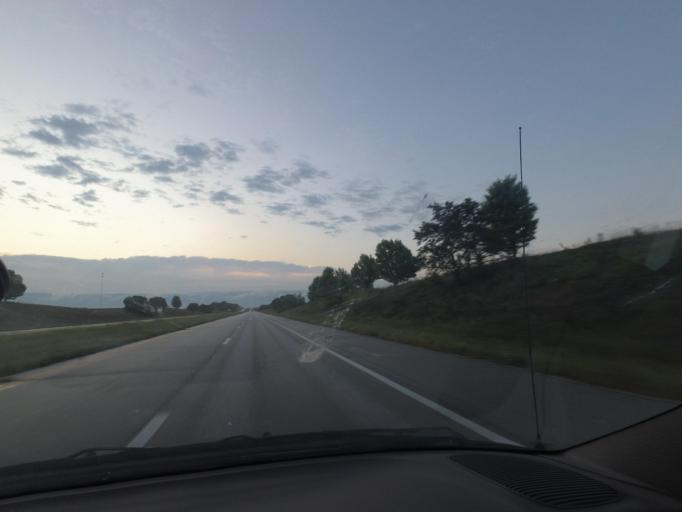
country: US
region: Missouri
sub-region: Macon County
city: Macon
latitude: 39.7585
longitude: -92.5482
